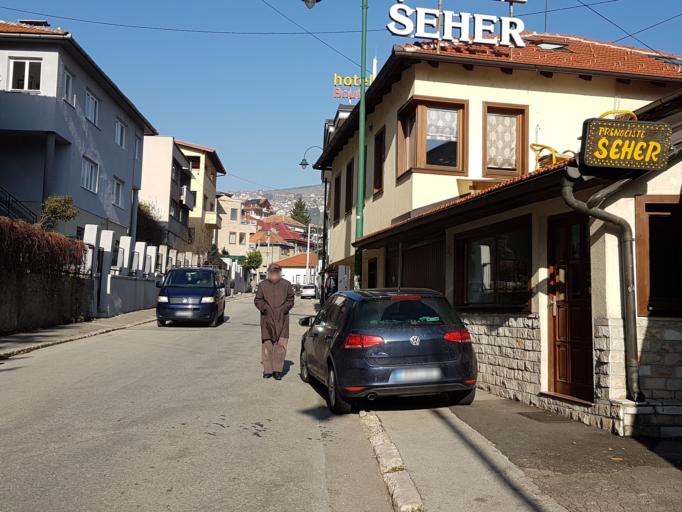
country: BA
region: Federation of Bosnia and Herzegovina
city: Kobilja Glava
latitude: 43.8625
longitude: 18.4314
